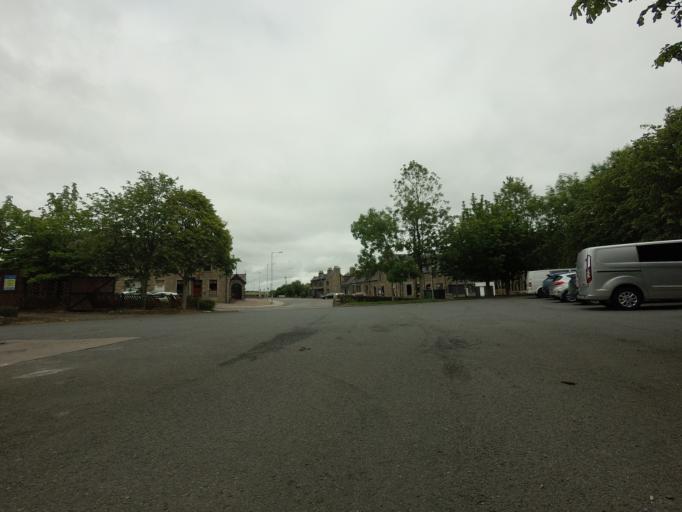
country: GB
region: Scotland
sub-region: Aberdeenshire
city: Mintlaw
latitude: 57.5212
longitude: -2.1258
